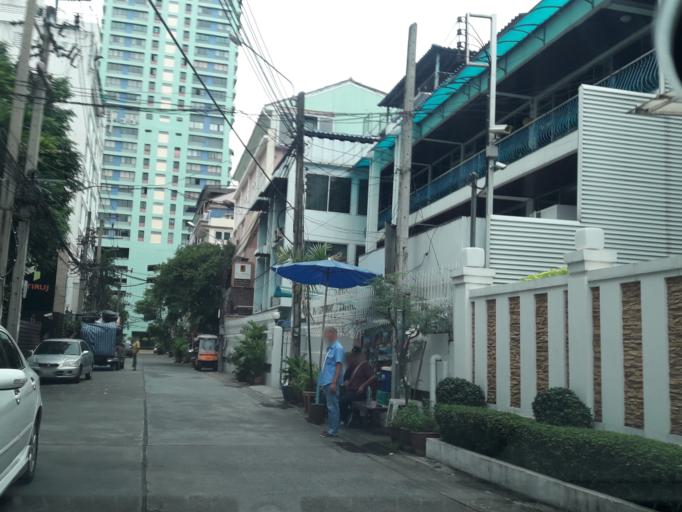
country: TH
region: Bangkok
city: Khlong Toei
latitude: 13.7359
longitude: 100.5559
